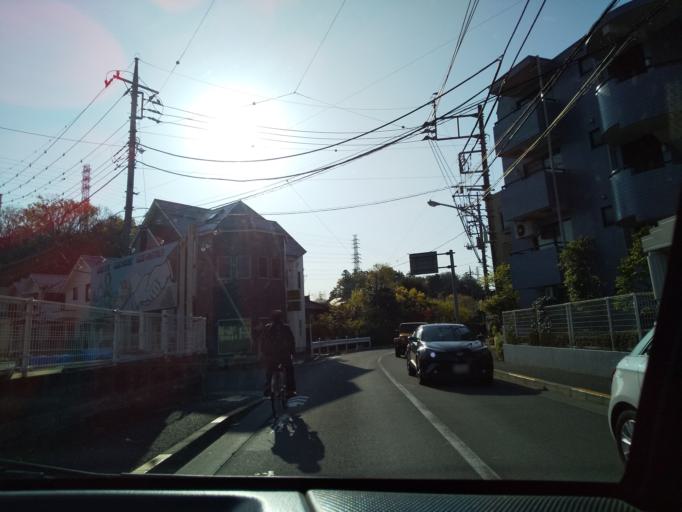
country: JP
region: Tokyo
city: Kokubunji
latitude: 35.7060
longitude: 139.4431
